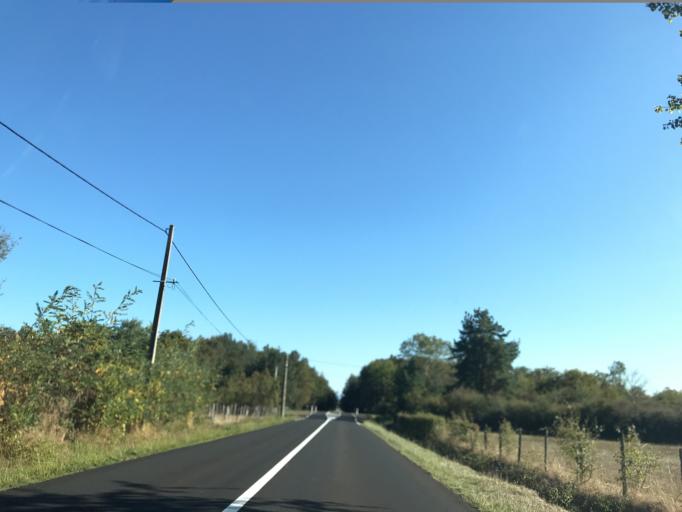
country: FR
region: Auvergne
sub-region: Departement du Puy-de-Dome
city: Peschadoires
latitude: 45.7864
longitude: 3.4654
